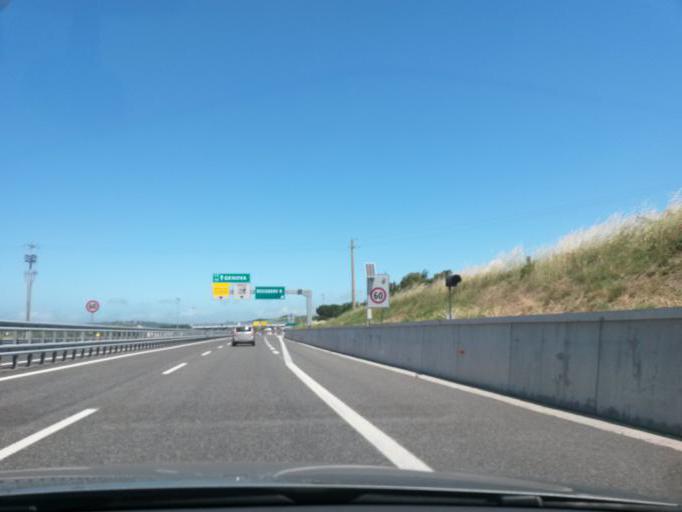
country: IT
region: Tuscany
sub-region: Provincia di Livorno
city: S.P. in Palazzi
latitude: 43.3656
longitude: 10.5054
